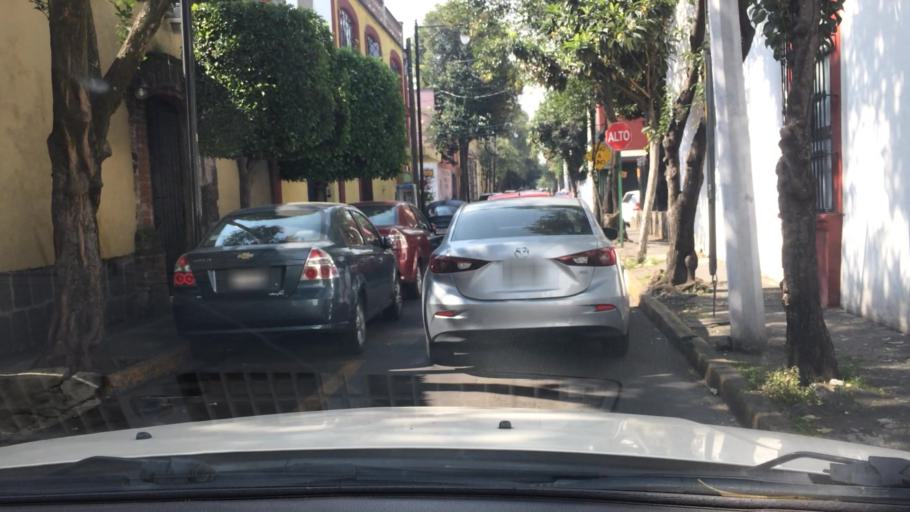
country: MX
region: Mexico City
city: Tlalpan
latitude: 19.2860
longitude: -99.1671
